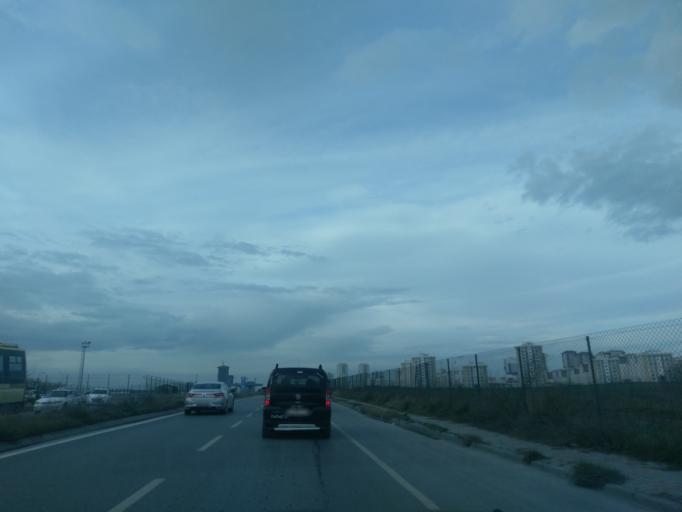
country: TR
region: Istanbul
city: Esenyurt
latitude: 41.0781
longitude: 28.6542
